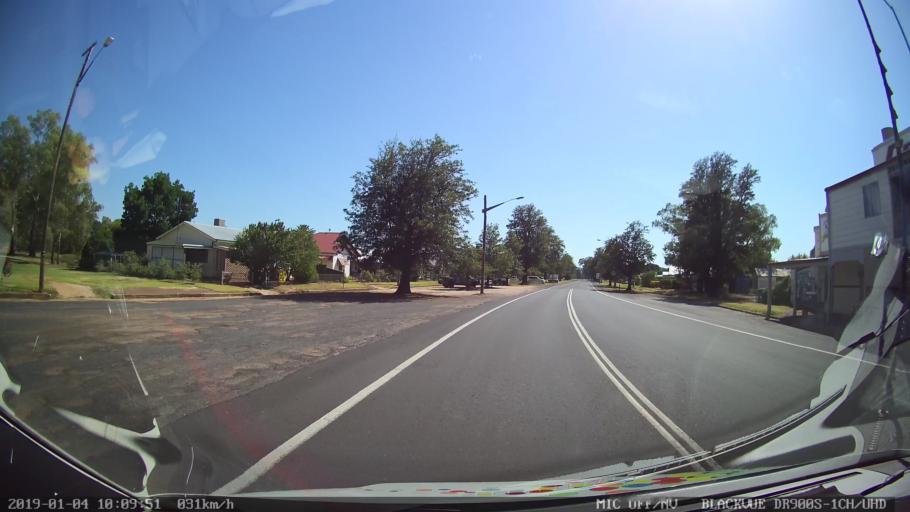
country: AU
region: New South Wales
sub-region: Cabonne
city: Canowindra
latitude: -33.4269
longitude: 148.3713
